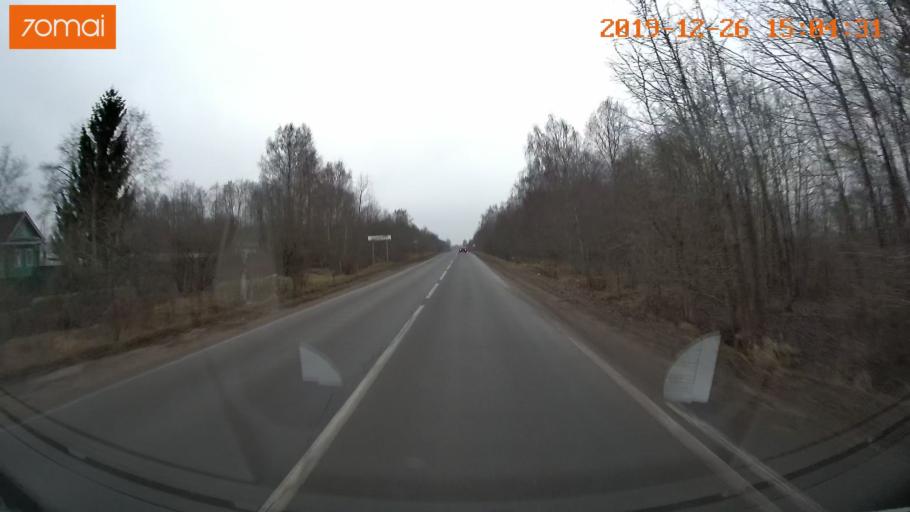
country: RU
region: Jaroslavl
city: Rybinsk
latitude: 58.1989
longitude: 38.8609
